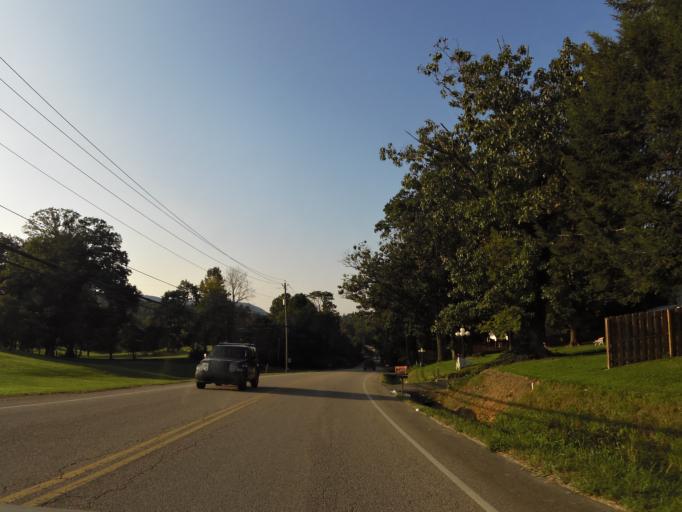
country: US
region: Tennessee
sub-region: Knox County
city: Mascot
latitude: 36.0741
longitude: -83.7434
